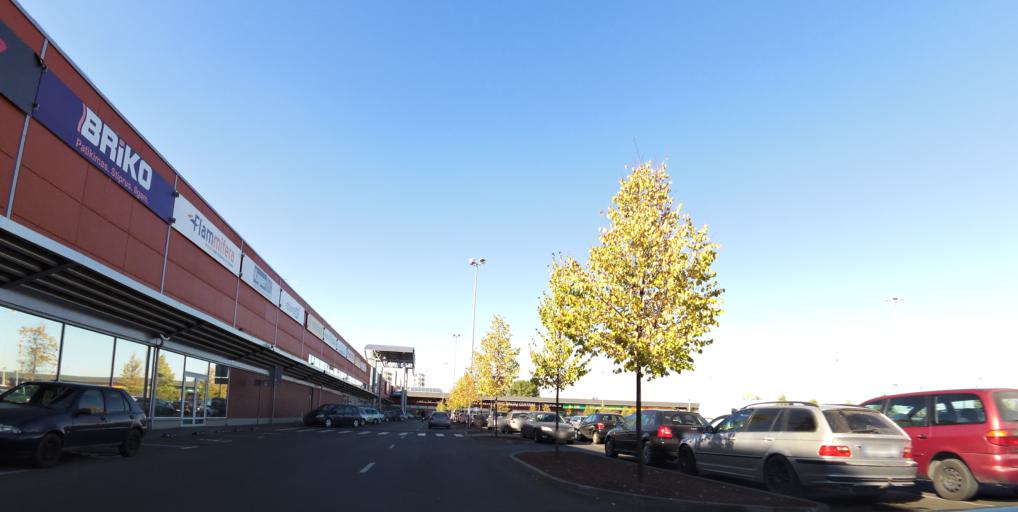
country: LT
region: Vilnius County
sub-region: Vilnius
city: Vilnius
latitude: 54.7097
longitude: 25.3016
